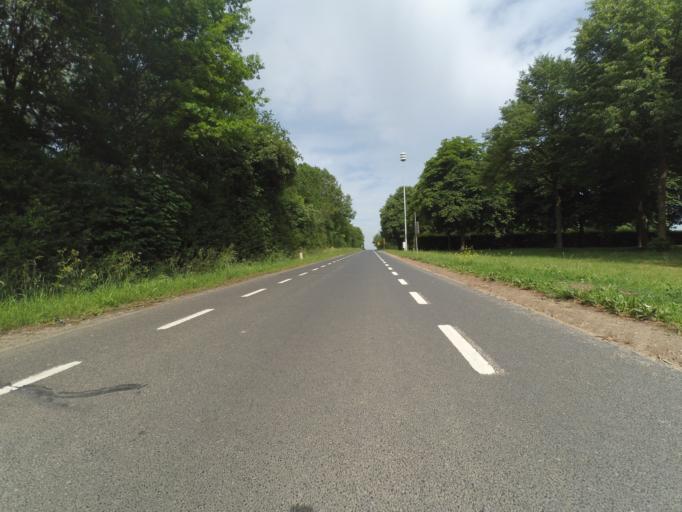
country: NL
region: Utrecht
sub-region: Gemeente Wijk bij Duurstede
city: Wijk bij Duurstede
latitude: 51.9526
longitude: 5.3564
